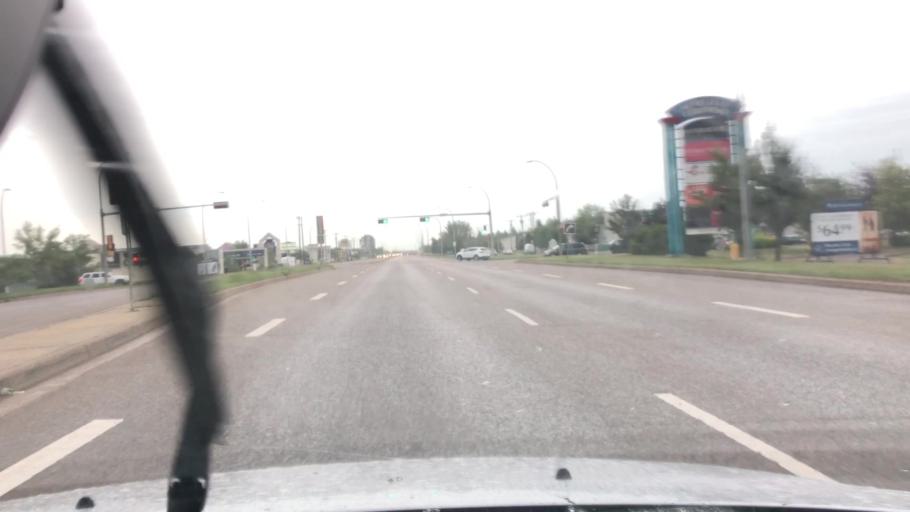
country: CA
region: Alberta
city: St. Albert
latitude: 53.5441
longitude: -113.6143
